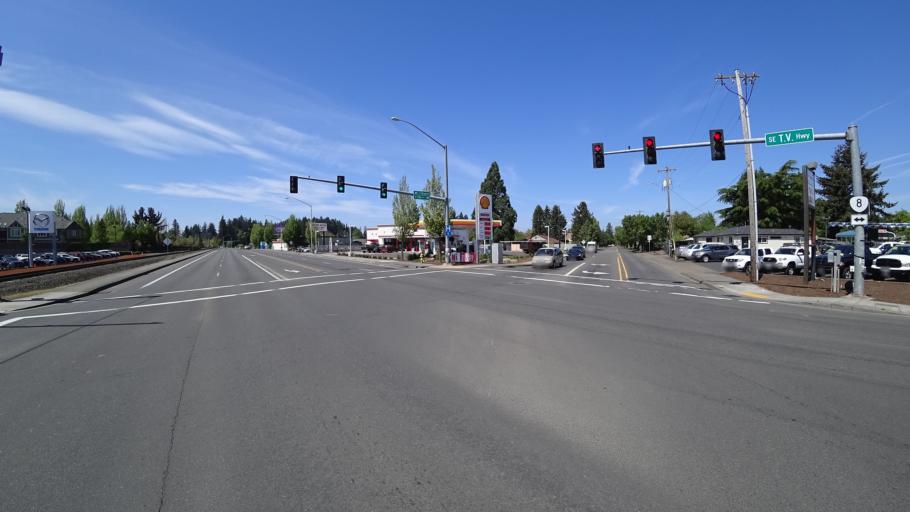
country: US
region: Oregon
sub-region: Washington County
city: Hillsboro
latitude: 45.5099
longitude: -122.9689
